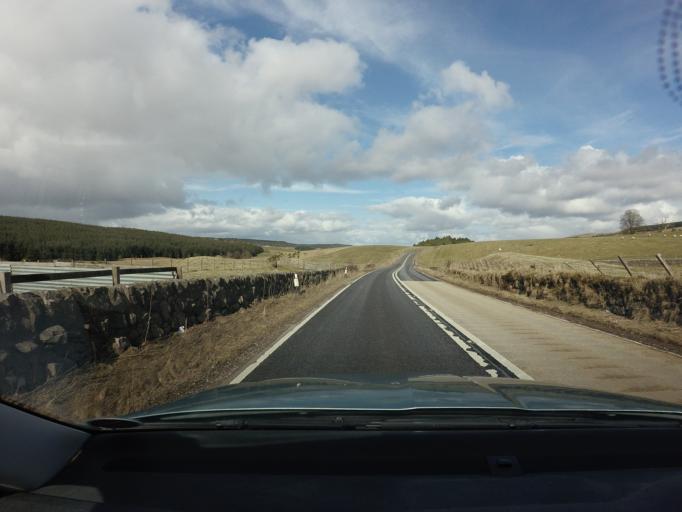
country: GB
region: Scotland
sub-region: South Lanarkshire
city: Douglas
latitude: 55.5401
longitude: -3.8676
